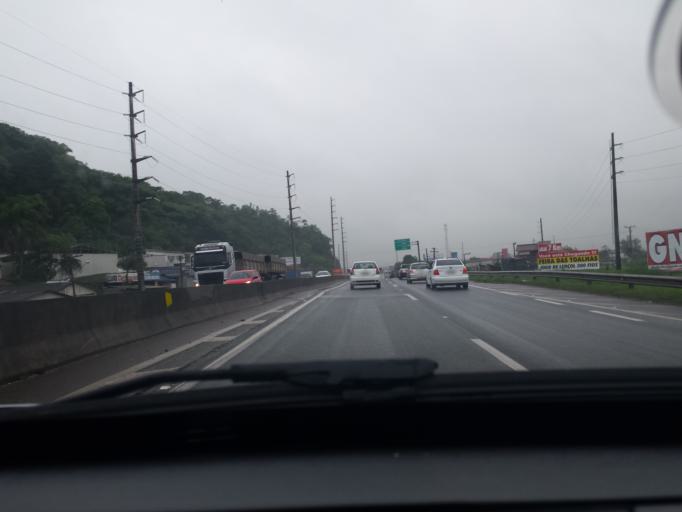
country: BR
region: Santa Catarina
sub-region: Itajai
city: Itajai
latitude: -26.9002
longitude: -48.7171
